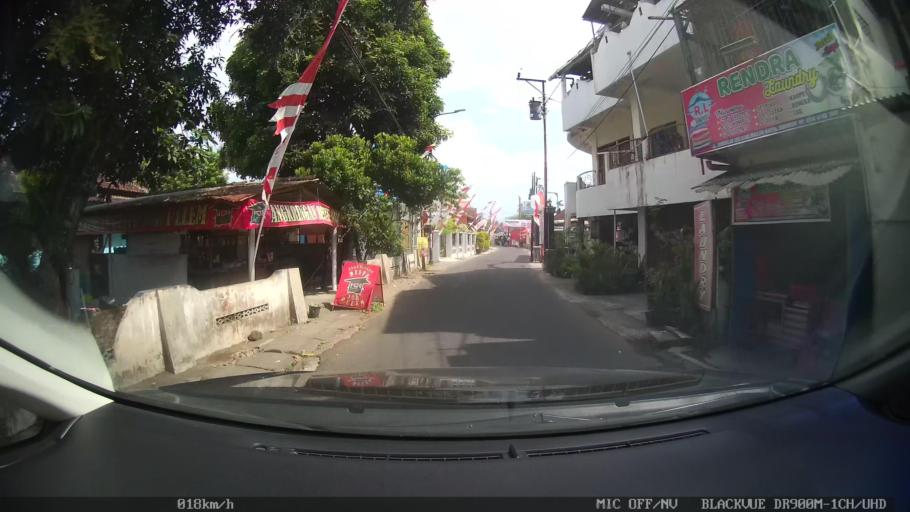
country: ID
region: Daerah Istimewa Yogyakarta
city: Gamping Lor
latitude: -7.8077
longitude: 110.3325
